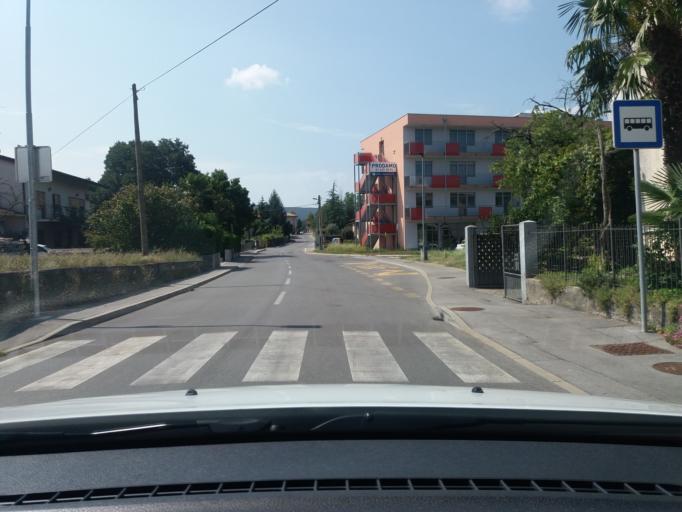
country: SI
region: Sempeter-Vrtojba
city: Vrtojba
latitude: 45.9070
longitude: 13.6296
